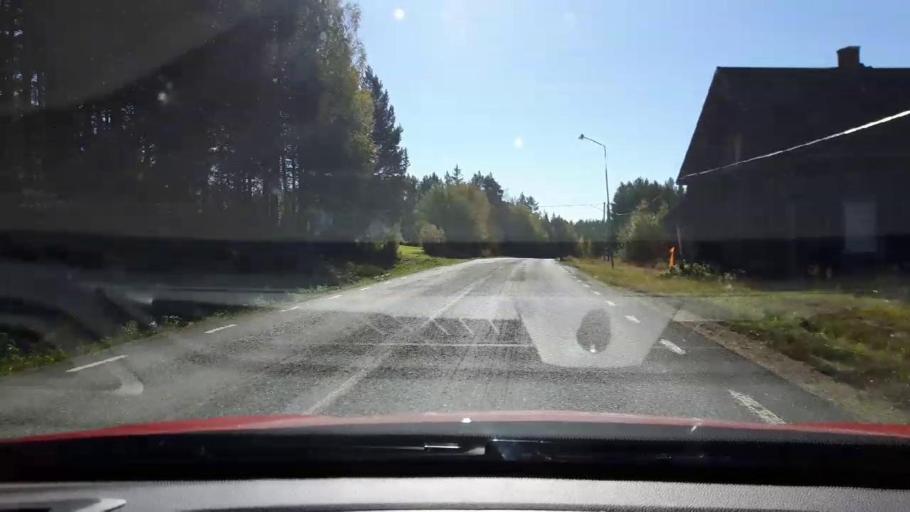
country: SE
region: Jaemtland
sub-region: Harjedalens Kommun
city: Sveg
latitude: 62.3267
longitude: 14.0606
